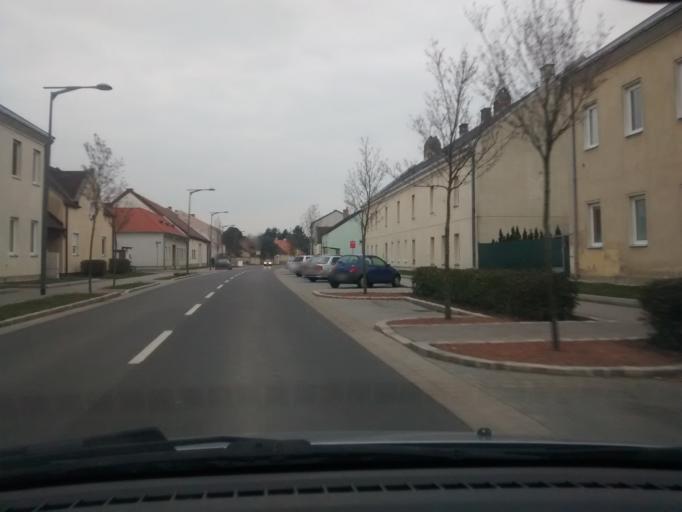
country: AT
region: Lower Austria
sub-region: Politischer Bezirk Bruck an der Leitha
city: Enzersdorf an der Fischa
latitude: 48.0950
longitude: 16.6059
